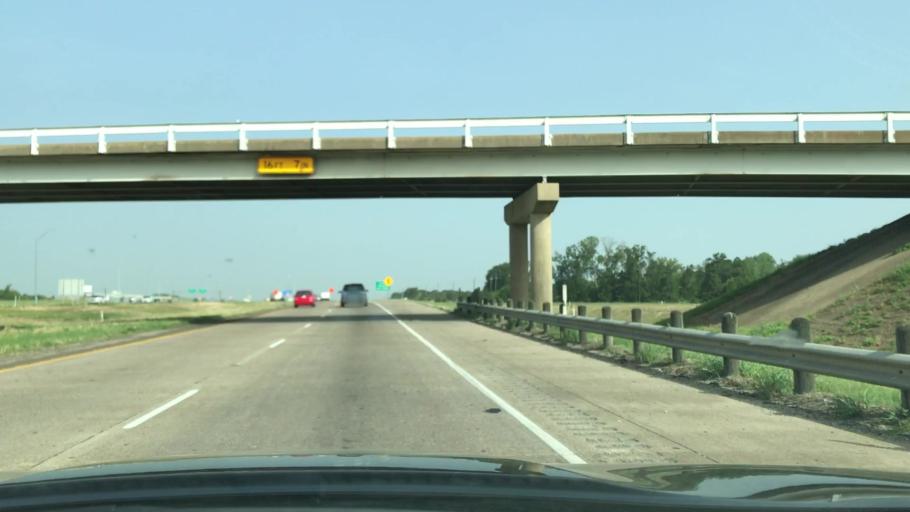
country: US
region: Texas
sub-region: Kaufman County
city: Terrell
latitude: 32.7126
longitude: -96.3002
